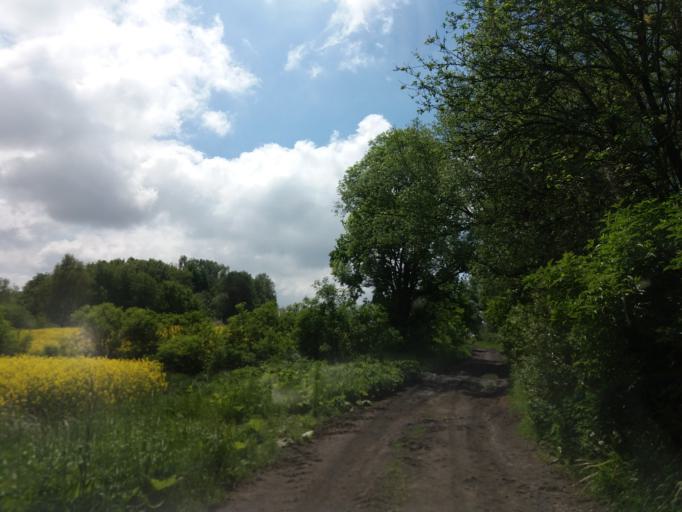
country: PL
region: West Pomeranian Voivodeship
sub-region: Powiat choszczenski
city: Recz
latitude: 53.2880
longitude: 15.5422
